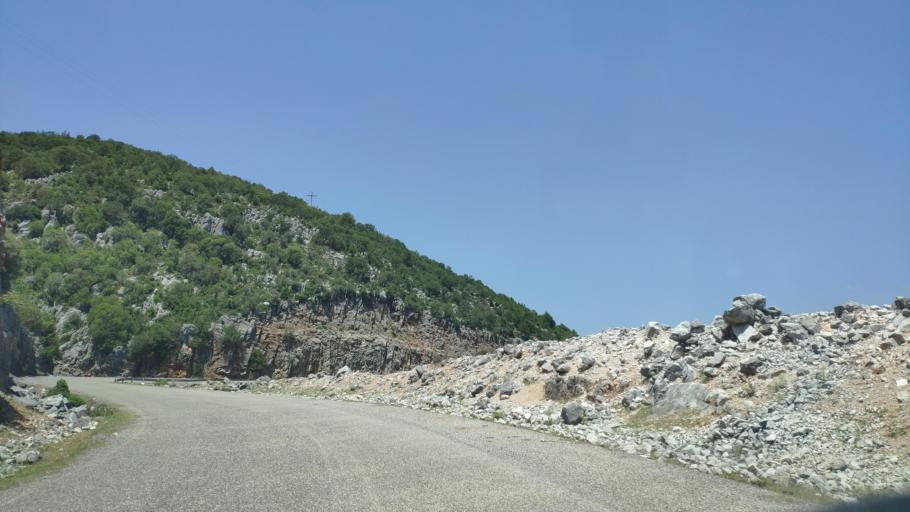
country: GR
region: Thessaly
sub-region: Nomos Kardhitsas
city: Anthiro
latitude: 39.1236
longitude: 21.3998
